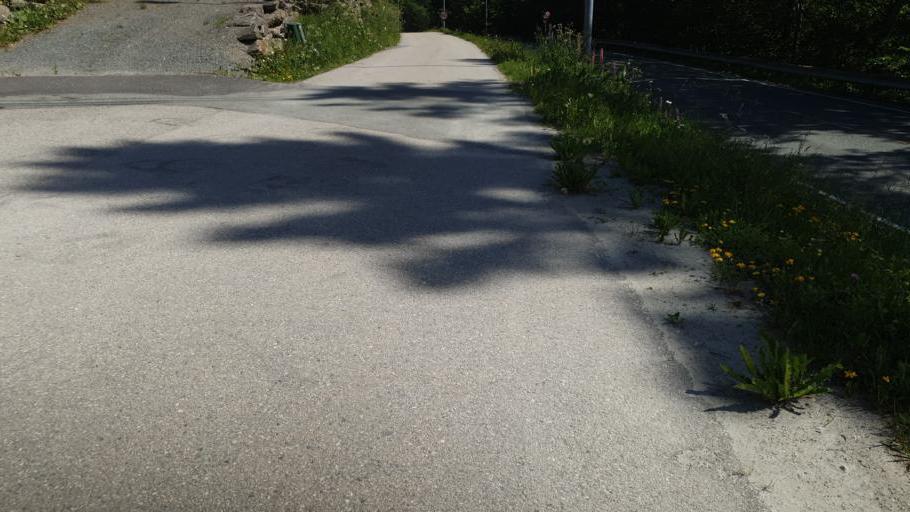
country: NO
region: Sor-Trondelag
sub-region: Trondheim
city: Trondheim
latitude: 63.5564
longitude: 10.2320
